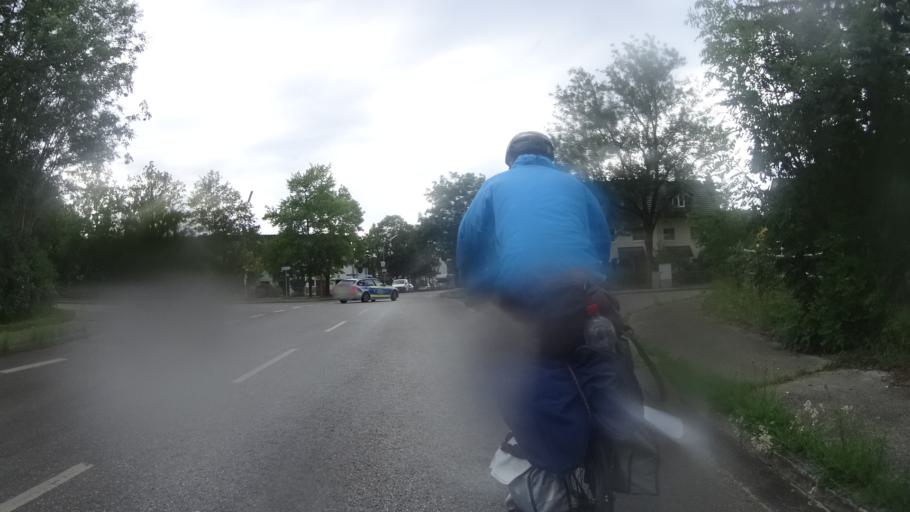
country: DE
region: Bavaria
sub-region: Upper Bavaria
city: Olching
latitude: 48.2152
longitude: 11.3031
